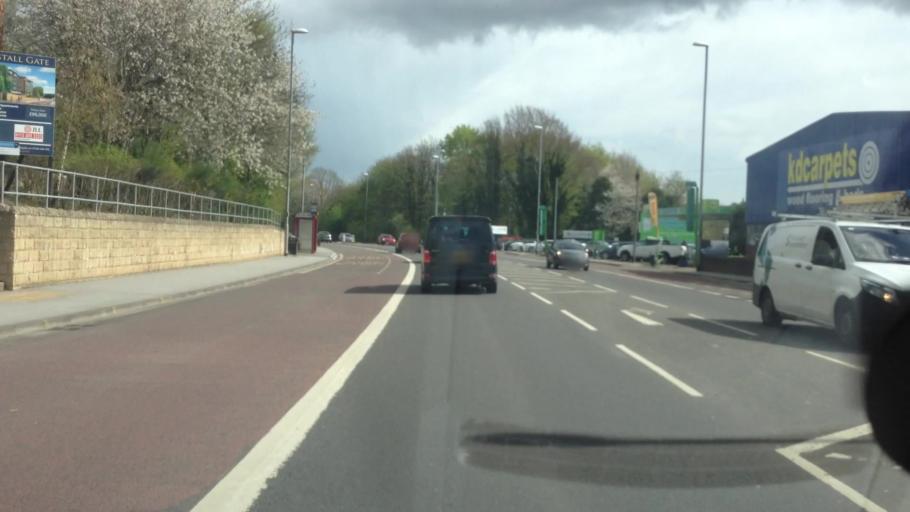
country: GB
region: England
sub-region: City and Borough of Leeds
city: Horsforth
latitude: 53.8123
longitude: -1.5984
